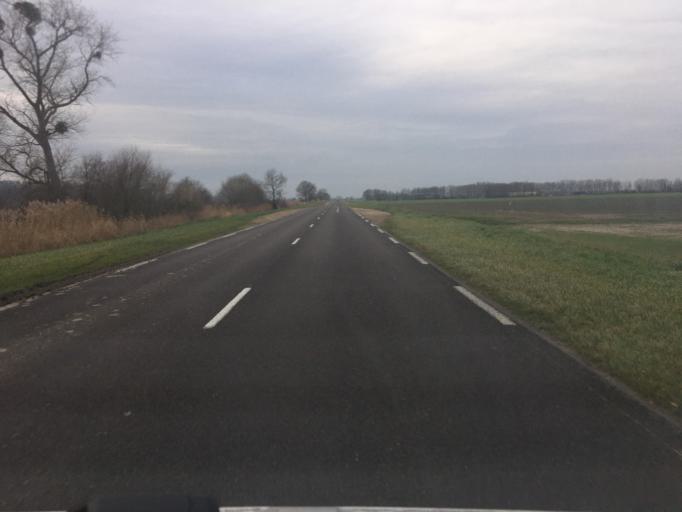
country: FR
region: Haute-Normandie
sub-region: Departement de la Seine-Maritime
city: Tancarville
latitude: 49.4513
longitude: 0.4491
